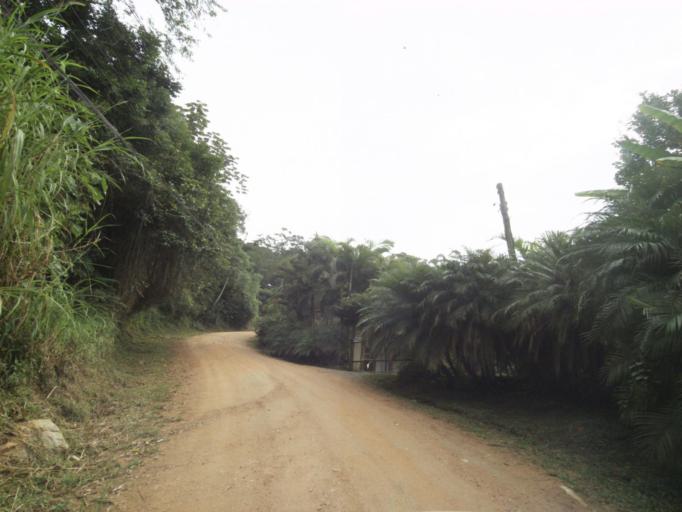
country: BR
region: Santa Catarina
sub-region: Pomerode
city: Pomerode
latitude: -26.7327
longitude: -49.1938
